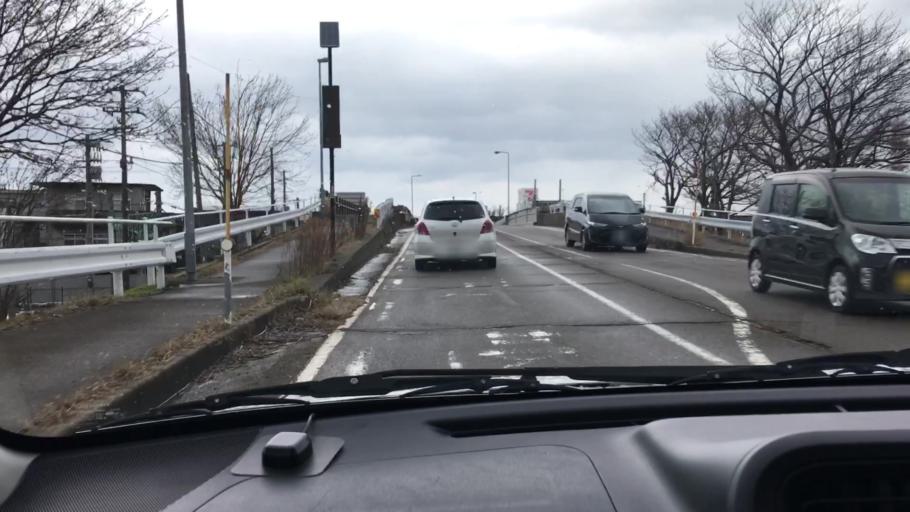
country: JP
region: Niigata
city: Joetsu
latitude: 37.1666
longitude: 138.2370
